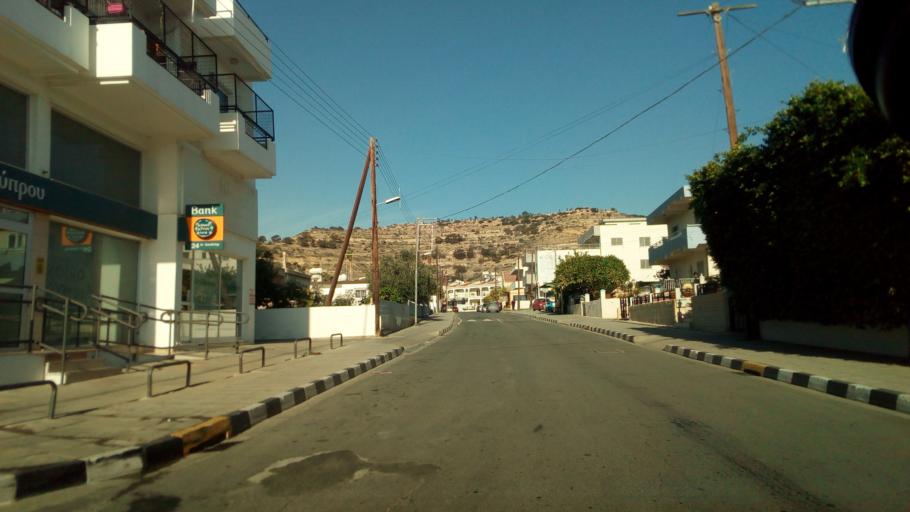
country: CY
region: Larnaka
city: Voroklini
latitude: 34.9845
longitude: 33.6541
